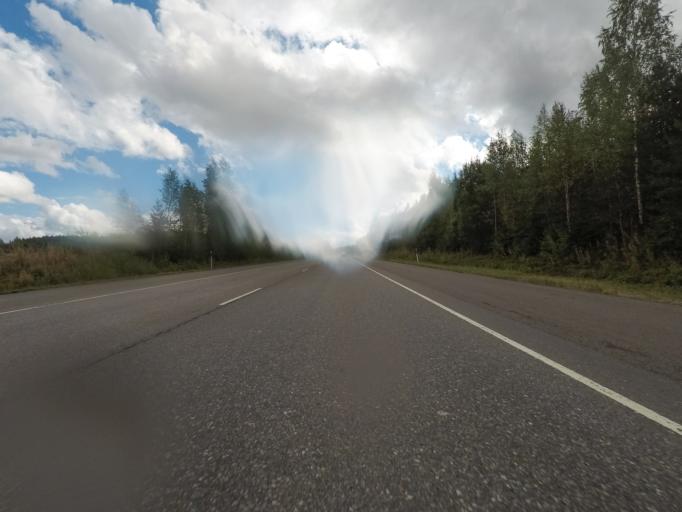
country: FI
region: Paijanne Tavastia
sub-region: Lahti
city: Heinola
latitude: 61.3187
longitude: 26.0429
